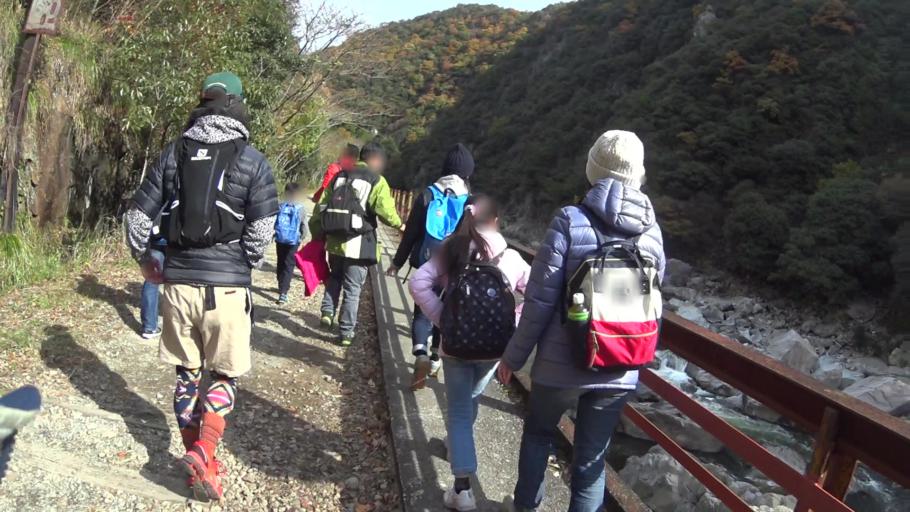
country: JP
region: Hyogo
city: Takarazuka
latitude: 34.8274
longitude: 135.3233
